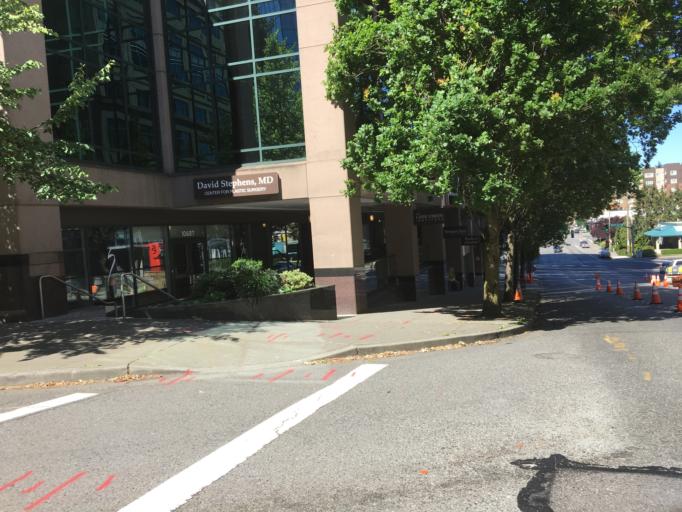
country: US
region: Washington
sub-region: King County
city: Bellevue
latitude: 47.6118
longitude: -122.1975
